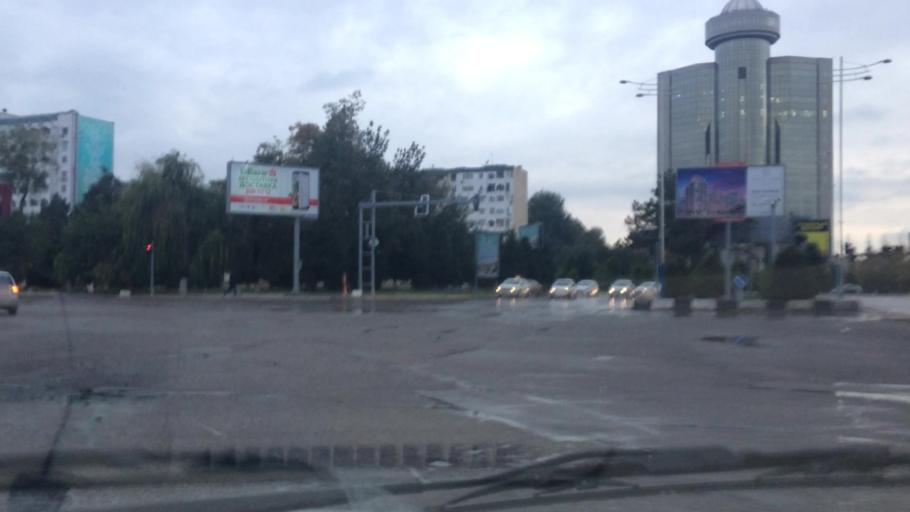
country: UZ
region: Toshkent Shahri
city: Tashkent
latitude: 41.3119
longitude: 69.2407
